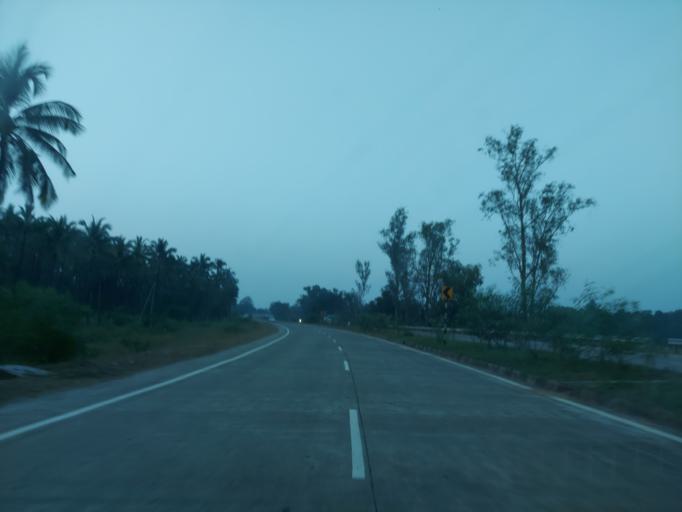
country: IN
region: Maharashtra
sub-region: Sindhudurg
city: Kudal
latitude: 16.0883
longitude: 73.7083
